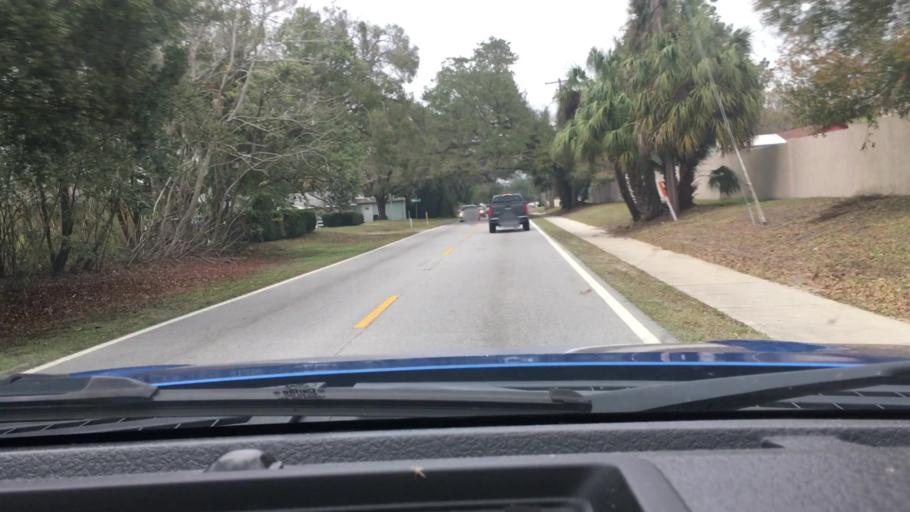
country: US
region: Florida
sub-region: Hillsborough County
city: Mango
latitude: 27.9658
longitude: -82.3104
